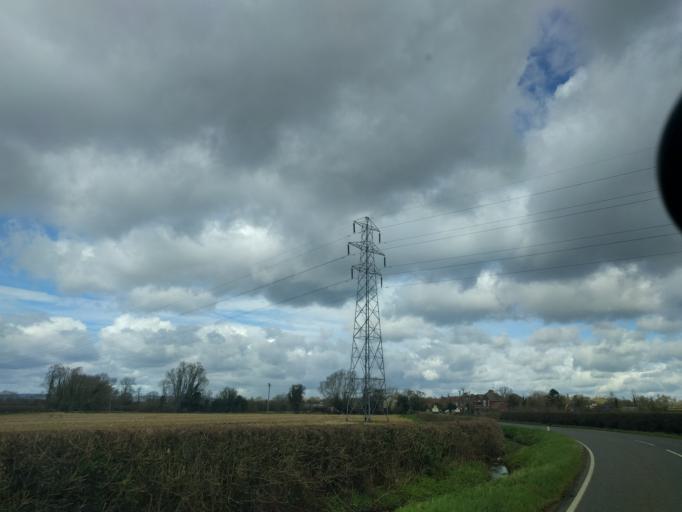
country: GB
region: England
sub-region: Gloucestershire
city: Stonehouse
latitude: 51.7373
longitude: -2.3201
